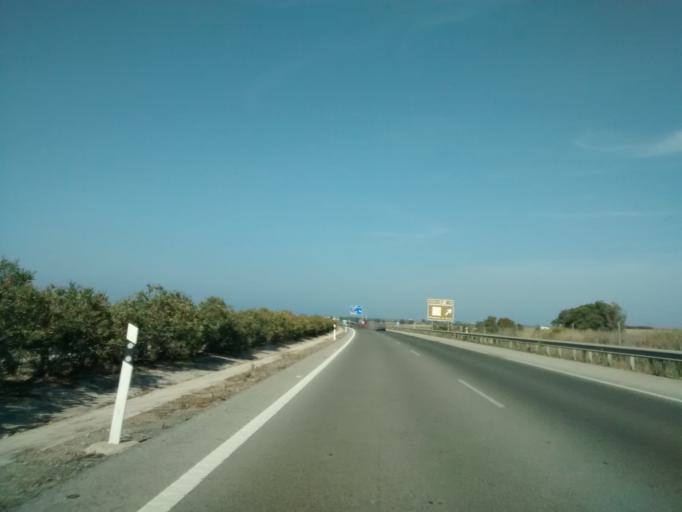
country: ES
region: Andalusia
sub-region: Provincia de Cadiz
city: Conil de la Frontera
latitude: 36.3552
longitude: -6.0836
